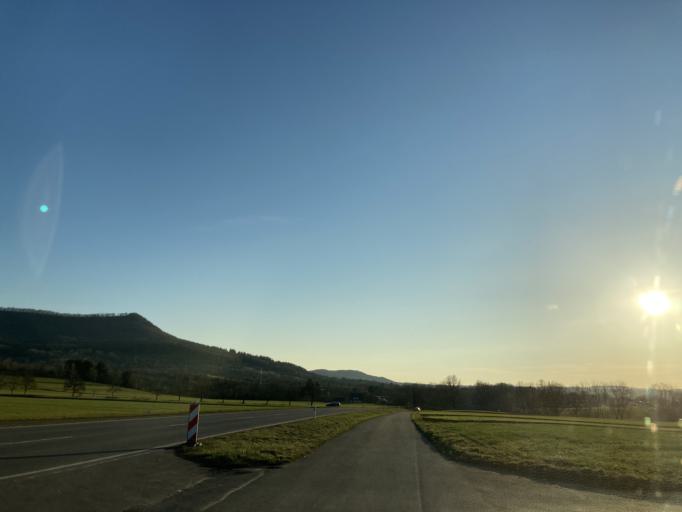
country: DE
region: Baden-Wuerttemberg
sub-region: Tuebingen Region
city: Nehren
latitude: 48.4097
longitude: 9.0921
